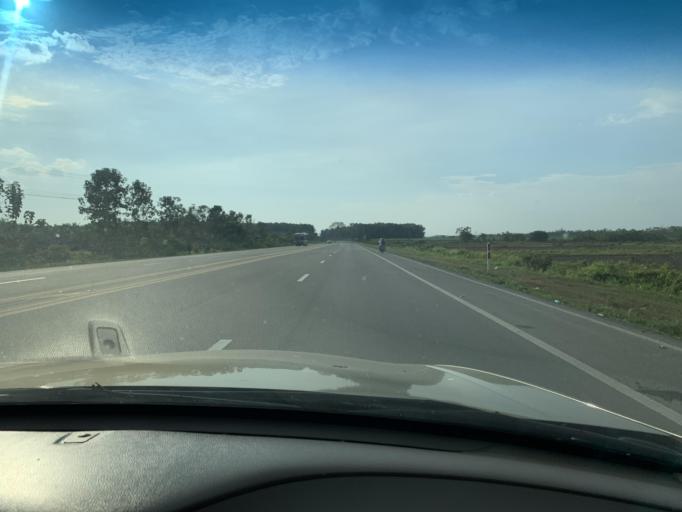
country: EC
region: Guayas
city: Coronel Marcelino Mariduena
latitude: -2.2840
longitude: -79.5150
